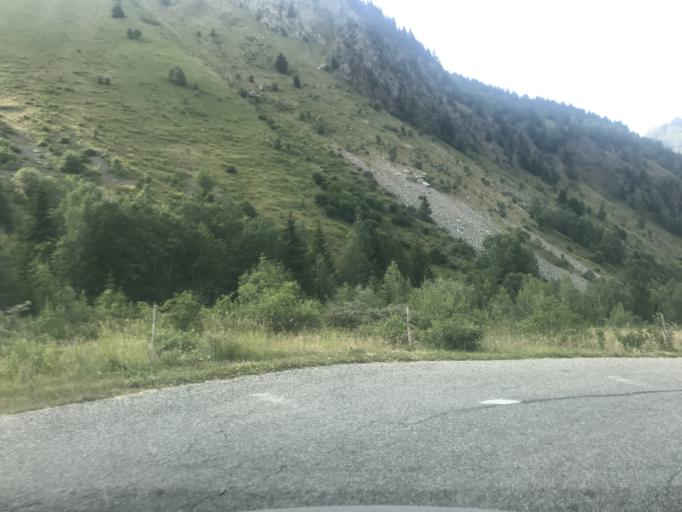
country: FR
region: Rhone-Alpes
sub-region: Departement de la Savoie
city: Saint-Etienne-de-Cuines
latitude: 45.2628
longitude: 6.1958
